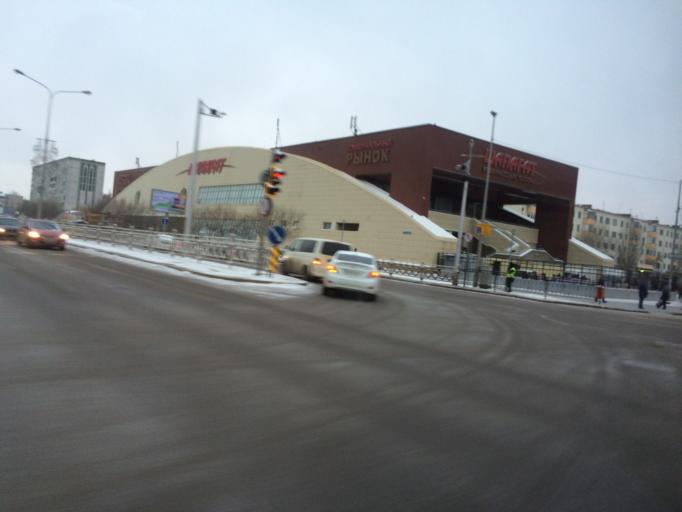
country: KZ
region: Astana Qalasy
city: Astana
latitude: 51.1785
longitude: 71.4367
